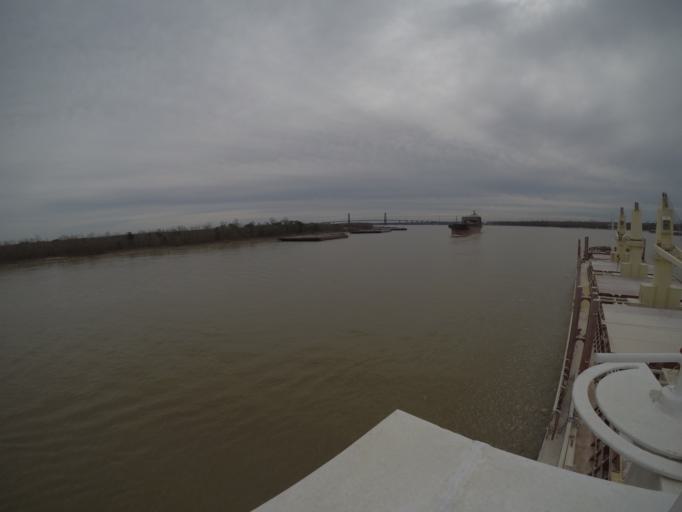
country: US
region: Louisiana
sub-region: Saint Charles Parish
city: New Sarpy
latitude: 29.9600
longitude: -90.3955
